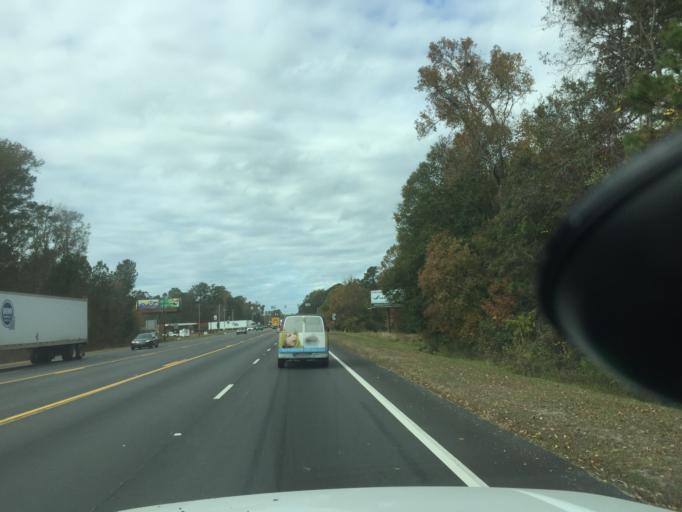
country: US
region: Georgia
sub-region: Chatham County
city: Garden City
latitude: 32.0921
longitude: -81.1940
